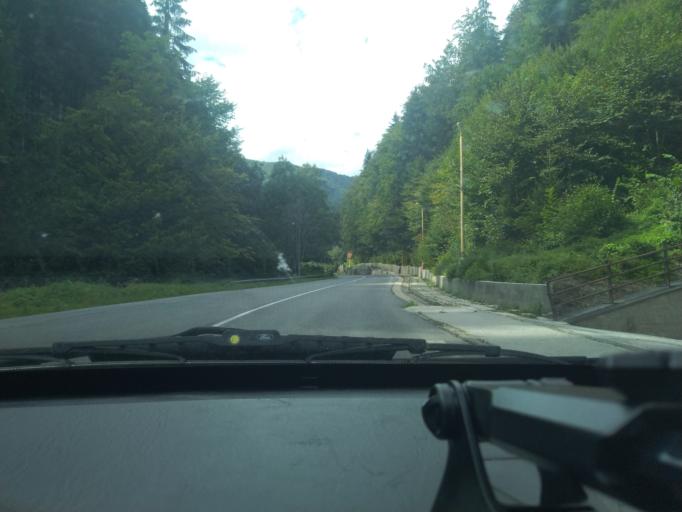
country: SK
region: Banskobystricky
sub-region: Okres Banska Bystrica
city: Banska Bystrica
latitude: 48.7954
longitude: 19.0710
